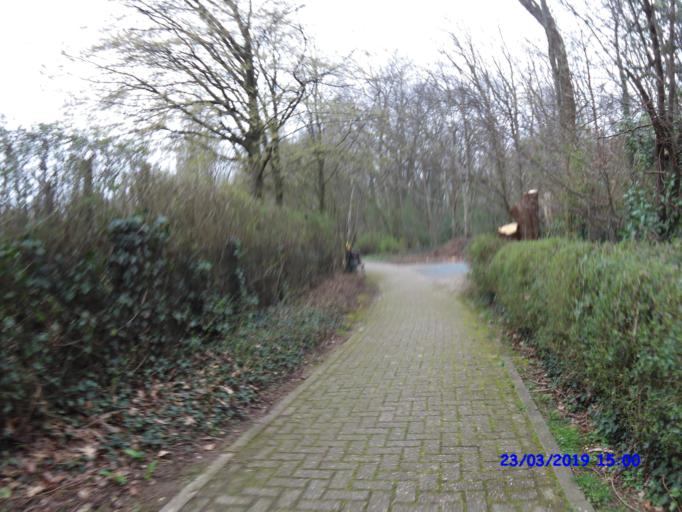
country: BE
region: Flanders
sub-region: Provincie Vlaams-Brabant
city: Dilbeek
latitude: 50.8579
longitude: 4.2915
